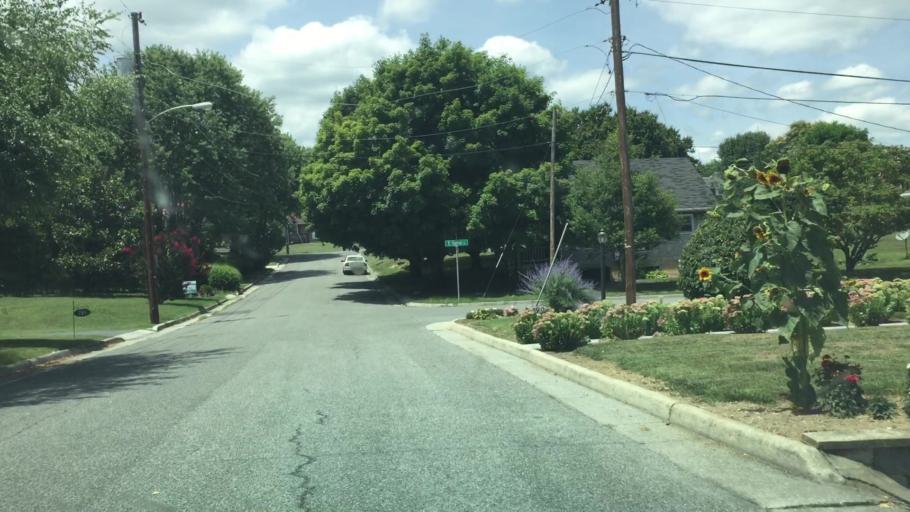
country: US
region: Virginia
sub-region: Wythe County
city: Wytheville
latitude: 36.9558
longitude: -81.0878
